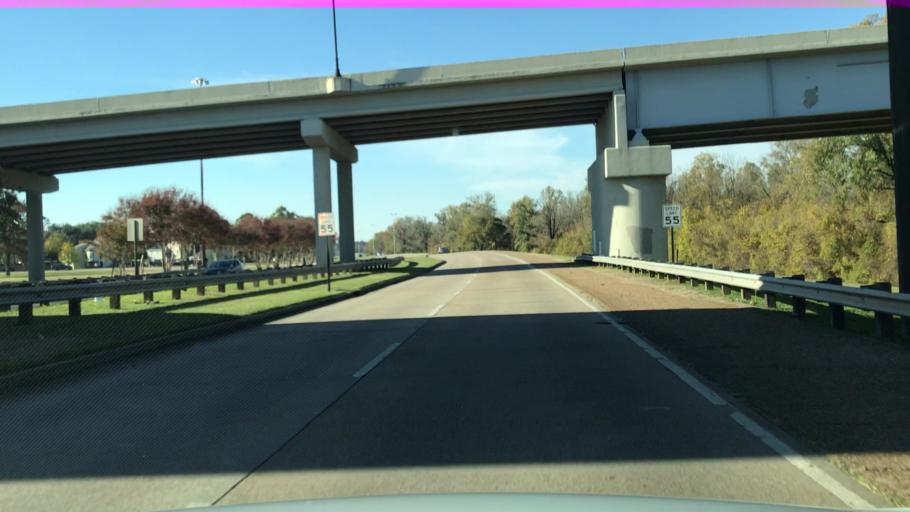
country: US
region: Louisiana
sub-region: Bossier Parish
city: Bossier City
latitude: 32.4908
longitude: -93.7007
